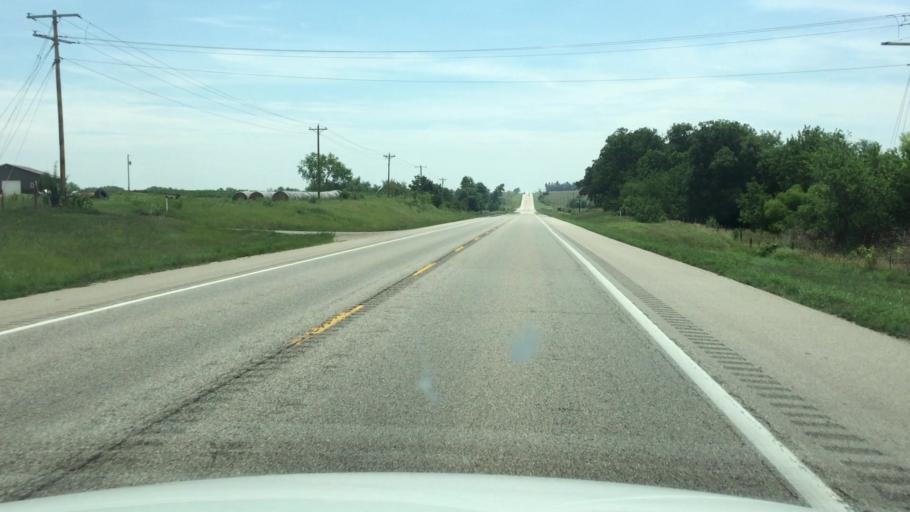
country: US
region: Kansas
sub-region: Brown County
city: Horton
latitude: 39.6897
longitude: -95.7304
